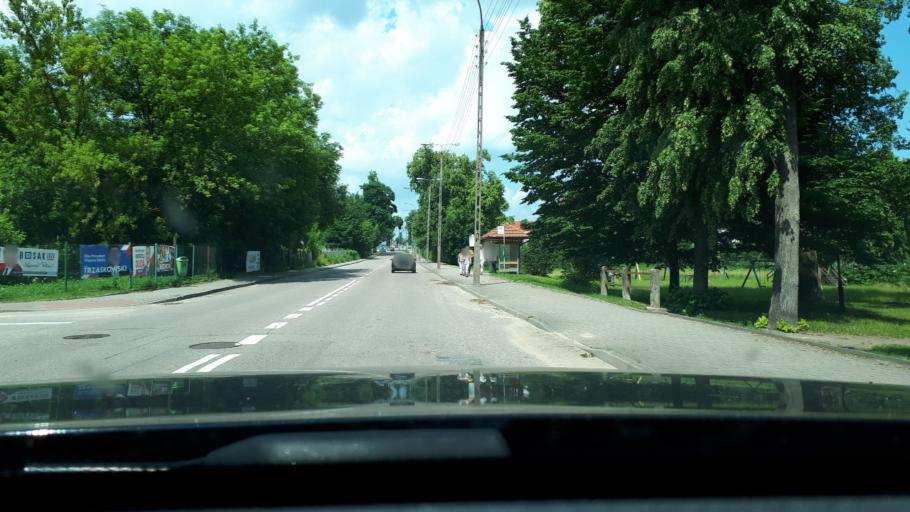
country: PL
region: Podlasie
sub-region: Powiat bialostocki
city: Suprasl
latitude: 53.2074
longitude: 23.3374
